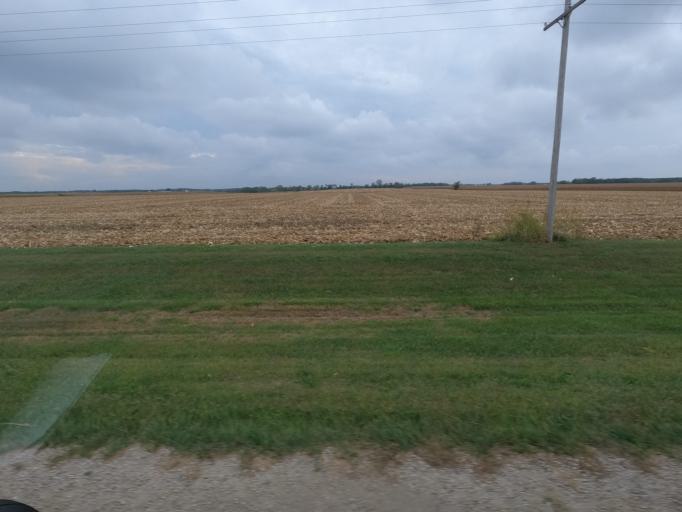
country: US
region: Iowa
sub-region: Van Buren County
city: Keosauqua
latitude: 40.8136
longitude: -91.8803
